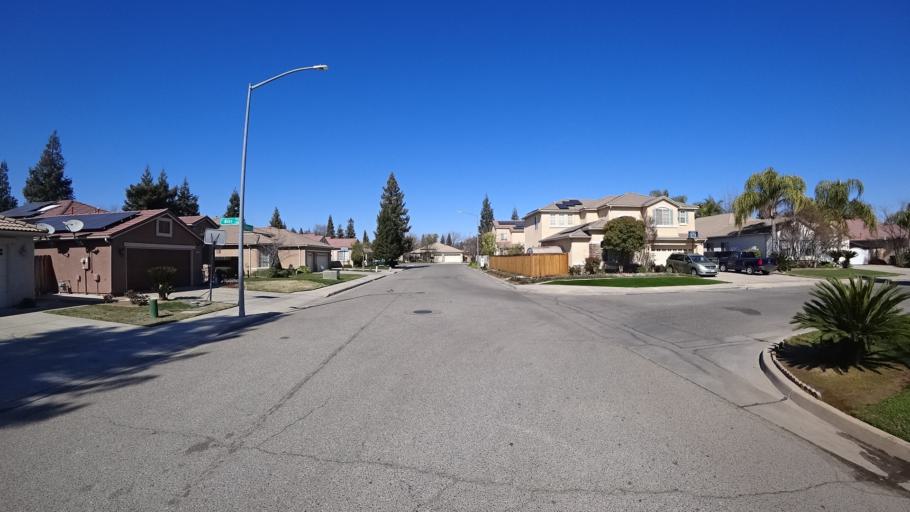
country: US
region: California
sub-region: Fresno County
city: Clovis
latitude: 36.8546
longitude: -119.7372
